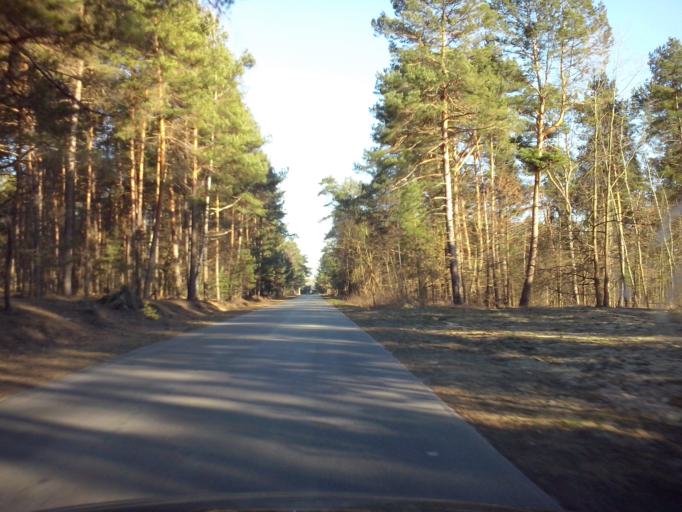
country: PL
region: Subcarpathian Voivodeship
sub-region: Powiat nizanski
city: Harasiuki
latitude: 50.5231
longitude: 22.4725
